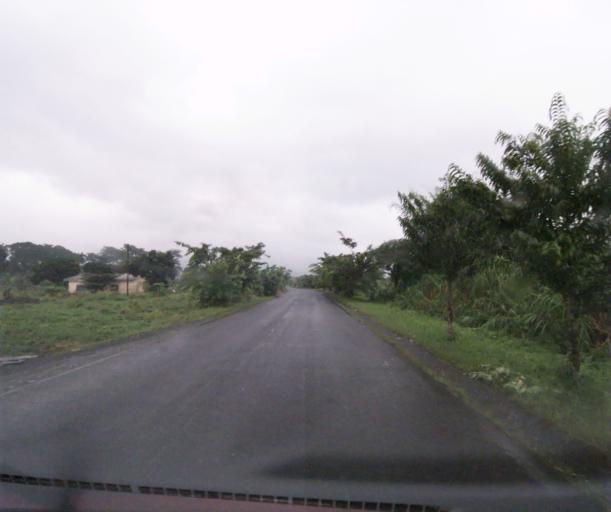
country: CM
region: South-West Province
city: Idenao
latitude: 4.2111
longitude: 8.9911
